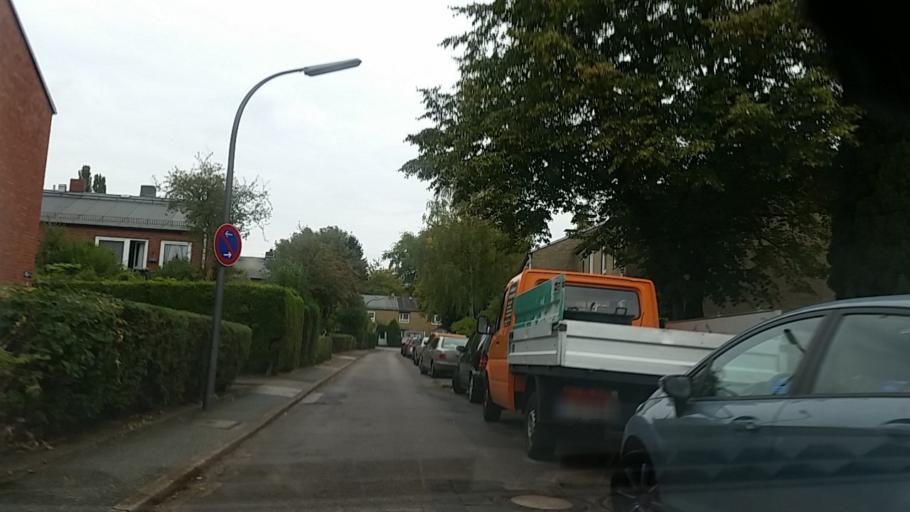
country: DE
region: Hamburg
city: Wandsbek
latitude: 53.5367
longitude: 10.1245
